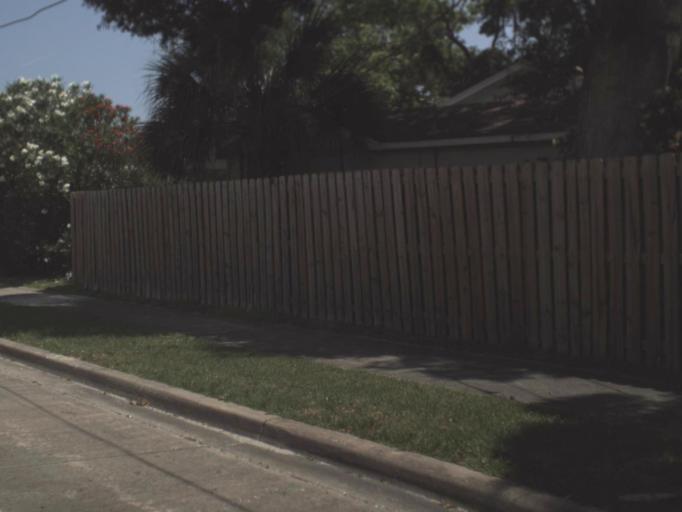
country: US
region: Florida
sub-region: Saint Johns County
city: Saint Augustine
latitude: 29.9199
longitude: -81.3248
